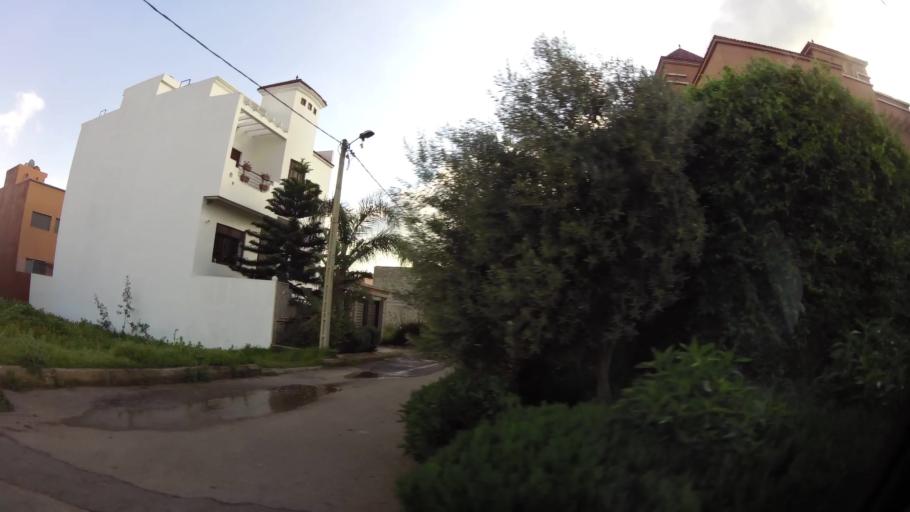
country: MA
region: Chaouia-Ouardigha
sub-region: Settat Province
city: Settat
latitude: 33.0096
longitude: -7.6383
